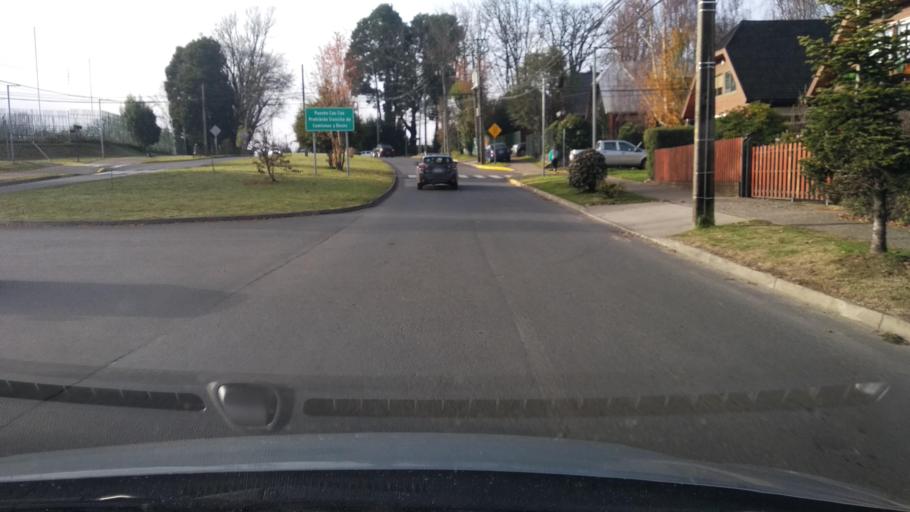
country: CL
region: Los Rios
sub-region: Provincia de Valdivia
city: Valdivia
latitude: -39.8088
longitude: -73.2567
